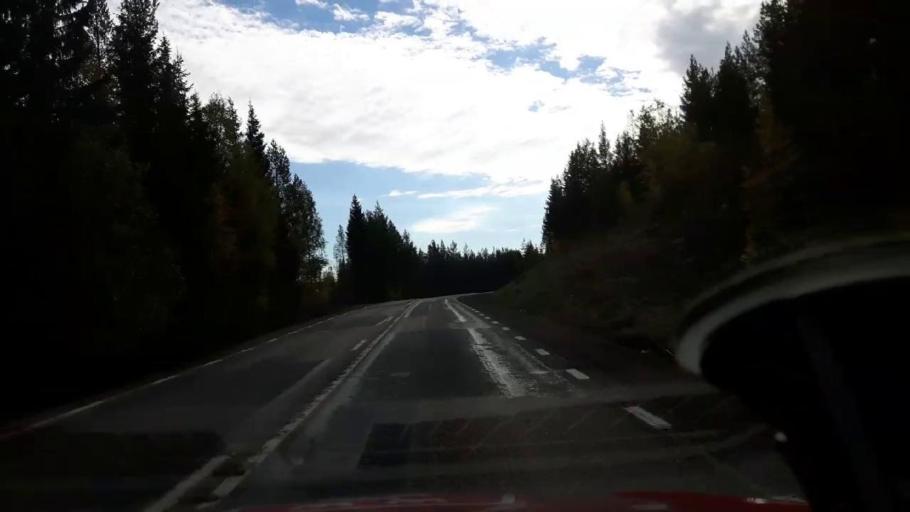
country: SE
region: Gaevleborg
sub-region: Ljusdals Kommun
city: Farila
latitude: 61.9459
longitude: 15.3763
